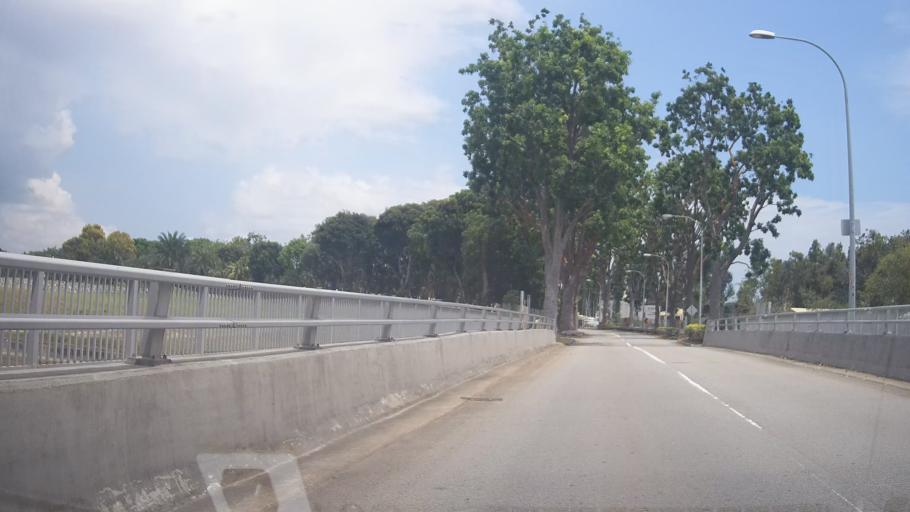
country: SG
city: Singapore
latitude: 1.3170
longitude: 103.9761
